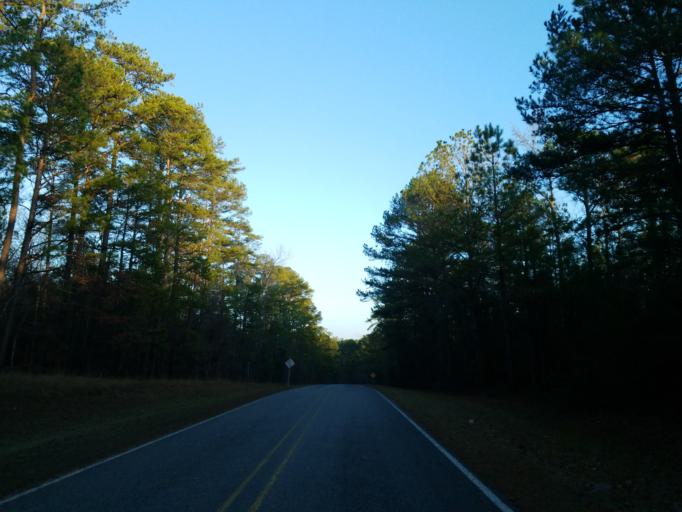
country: US
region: Mississippi
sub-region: Clarke County
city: Stonewall
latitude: 32.2635
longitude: -88.7987
